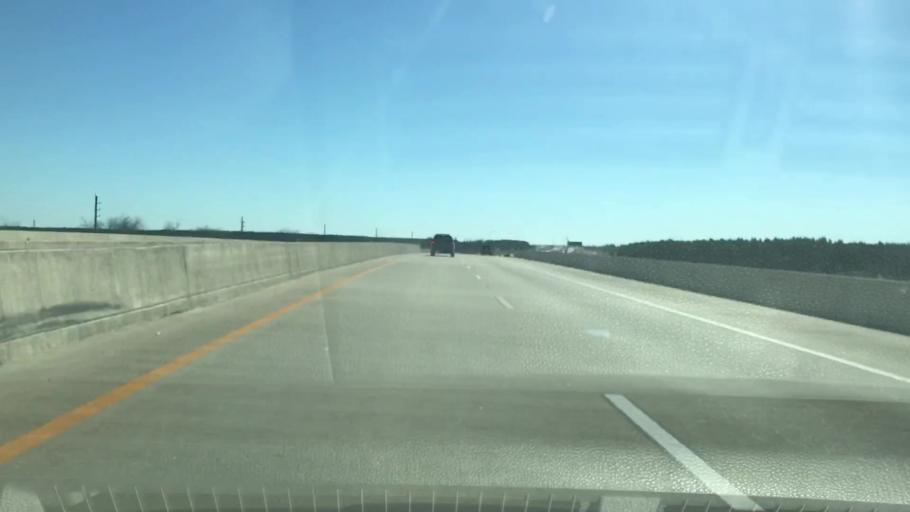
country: US
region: Texas
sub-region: Harris County
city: Cypress
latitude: 29.9045
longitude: -95.7587
